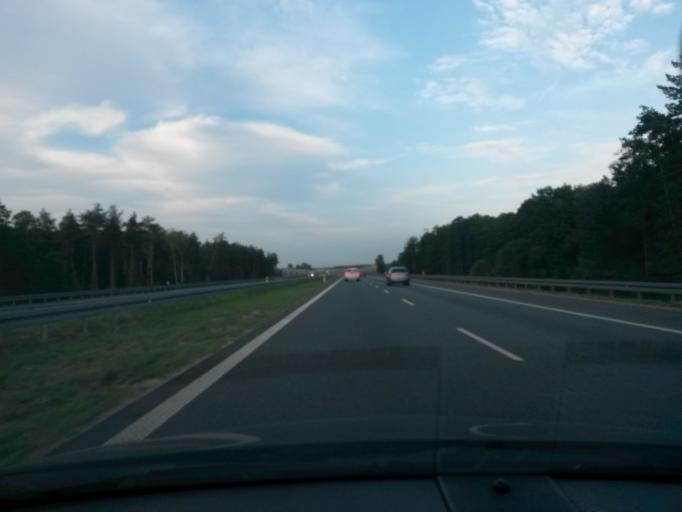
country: PL
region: Lodz Voivodeship
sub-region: Powiat skierniewicki
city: Bolimow
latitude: 52.0561
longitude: 20.1350
